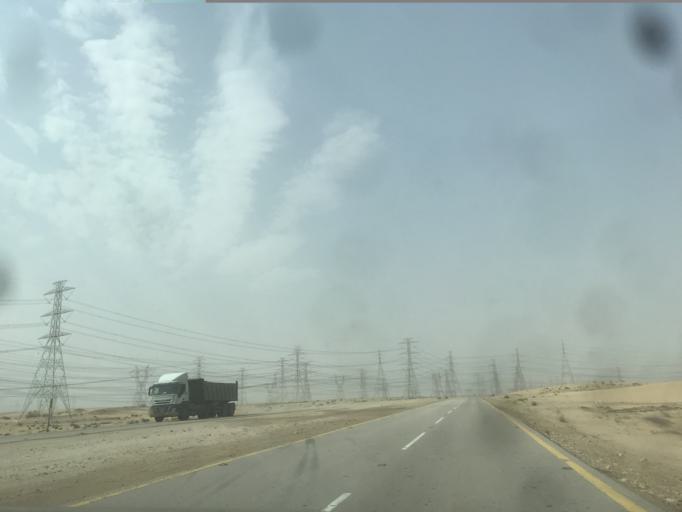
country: SA
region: Eastern Province
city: Abqaiq
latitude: 25.9072
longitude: 49.9204
